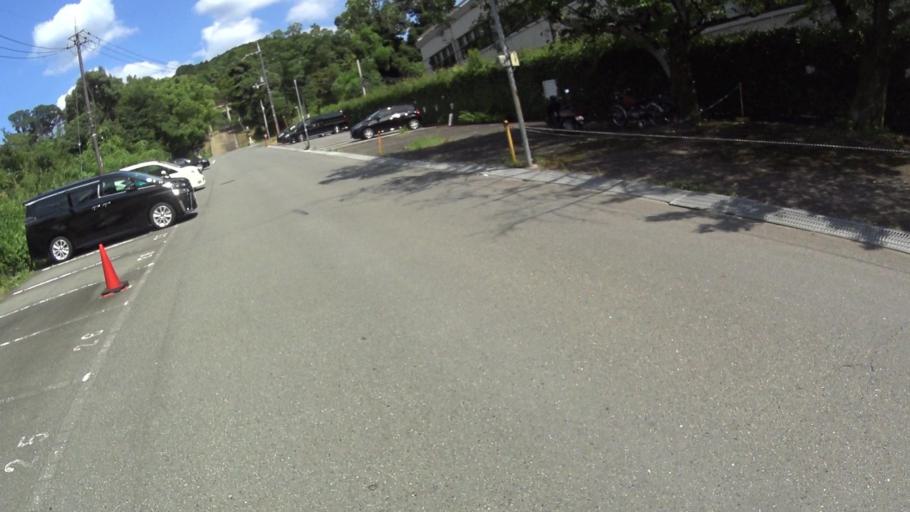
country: RU
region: Rostov
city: Remontnoye
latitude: 46.4990
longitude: 43.7772
